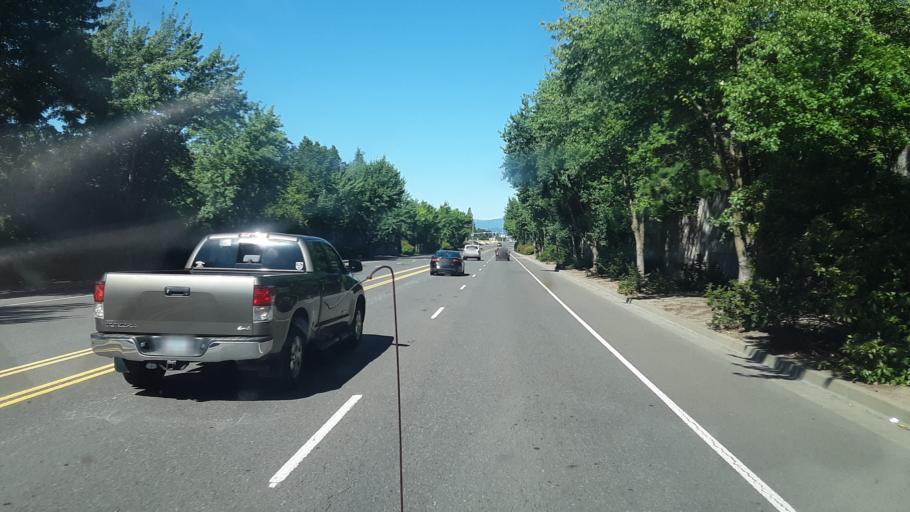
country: US
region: Oregon
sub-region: Josephine County
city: Grants Pass
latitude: 42.4263
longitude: -123.3240
